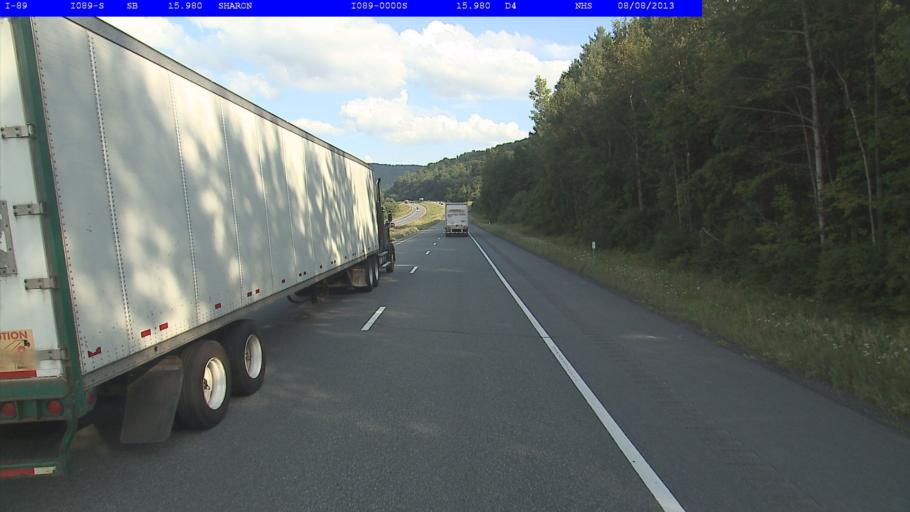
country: US
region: Vermont
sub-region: Windsor County
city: Woodstock
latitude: 43.7899
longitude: -72.4992
